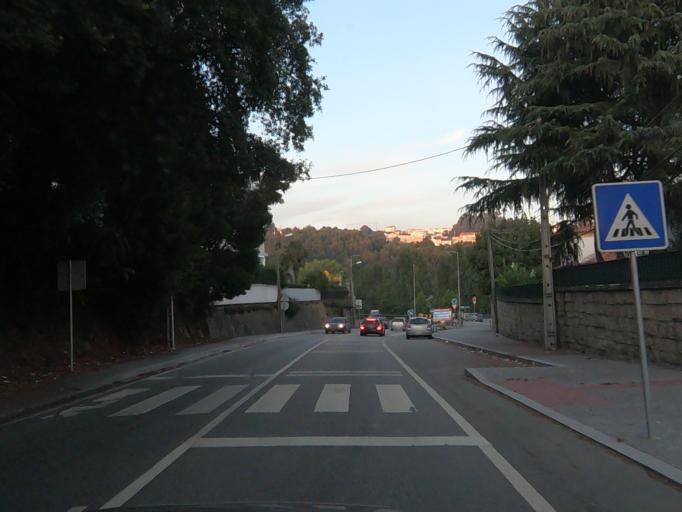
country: PT
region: Porto
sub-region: Gondomar
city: Valbom
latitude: 41.1264
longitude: -8.5609
